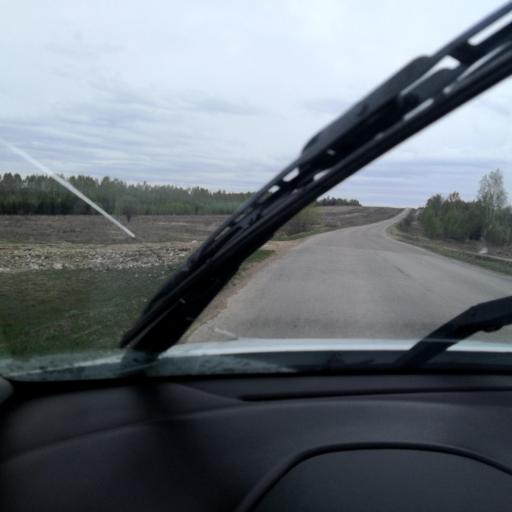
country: RU
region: Bashkortostan
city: Pavlovka
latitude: 55.3787
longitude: 56.4234
